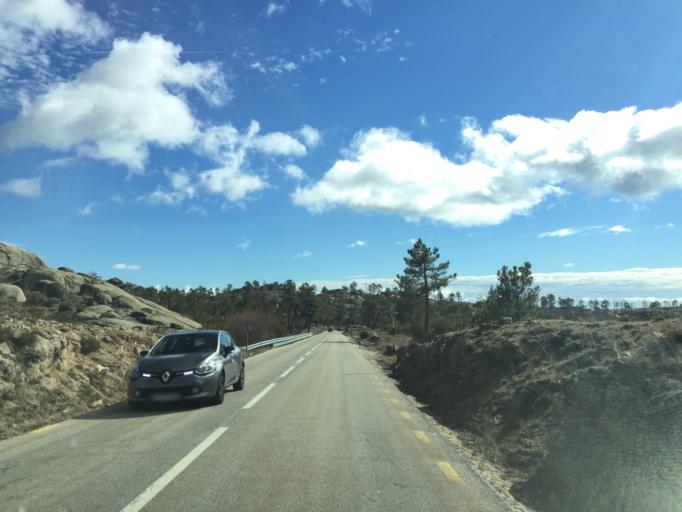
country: PT
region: Castelo Branco
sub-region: Covilha
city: Covilha
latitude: 40.3041
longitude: -7.5366
